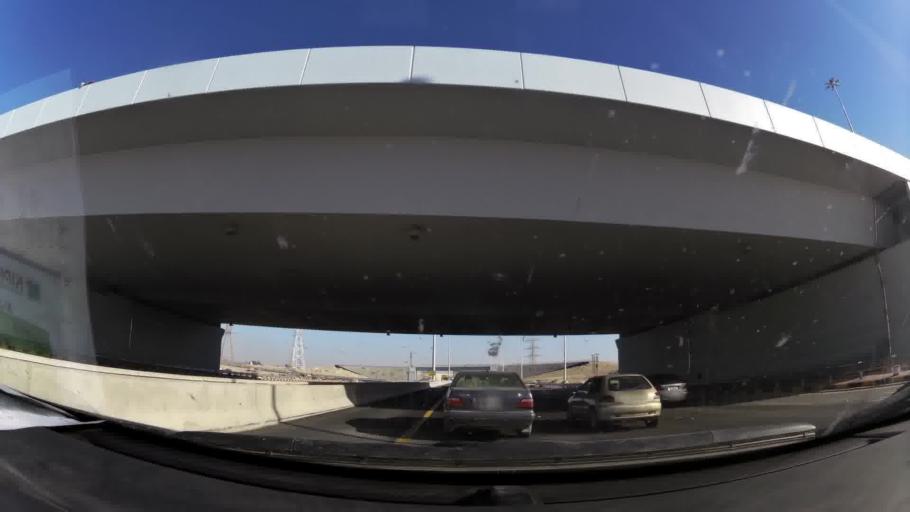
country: KW
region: Muhafazat al Jahra'
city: Al Jahra'
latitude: 29.2837
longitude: 47.7847
